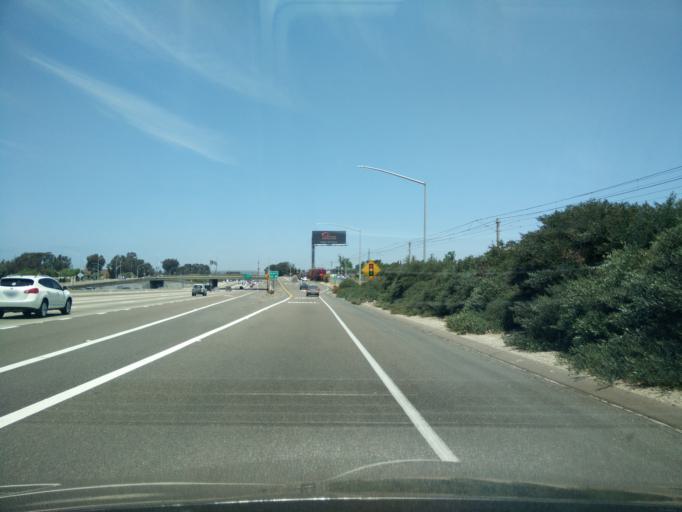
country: US
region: California
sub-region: San Diego County
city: Chula Vista
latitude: 32.6268
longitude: -117.0947
